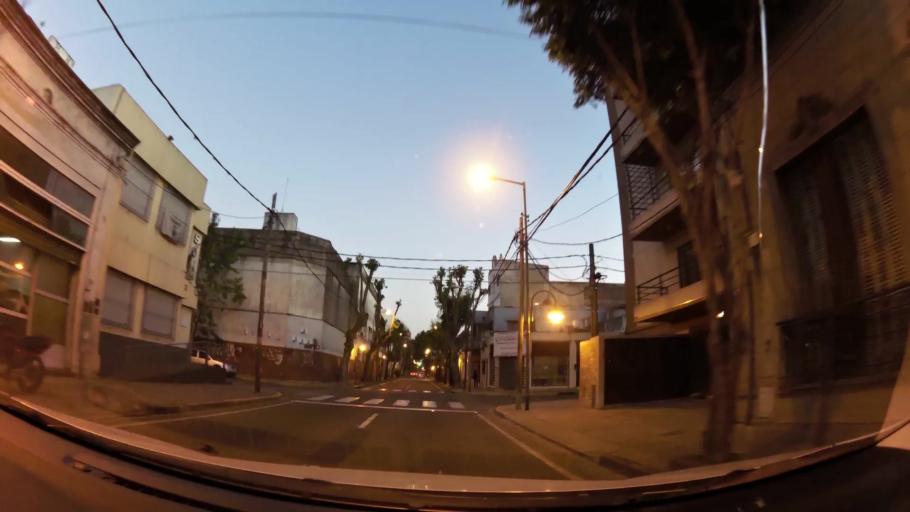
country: AR
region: Buenos Aires
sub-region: Partido de Tigre
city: Tigre
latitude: -34.4343
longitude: -58.5637
